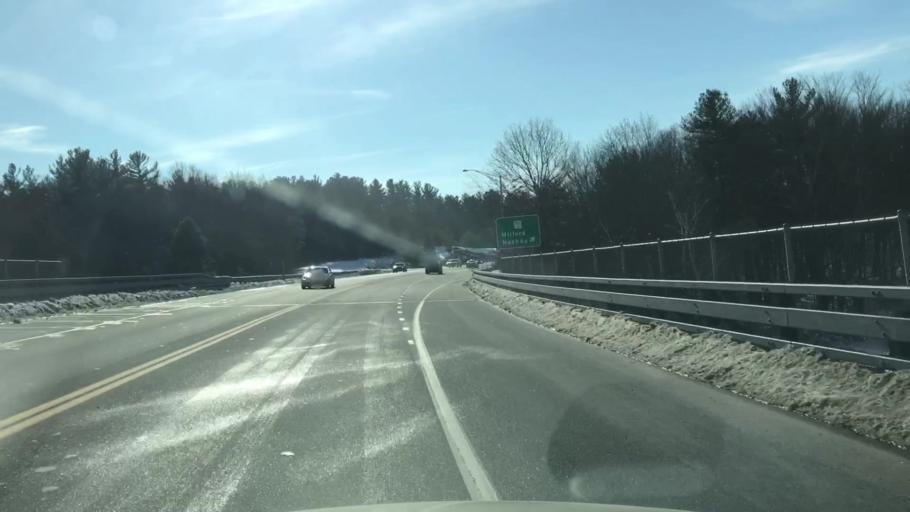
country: US
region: New Hampshire
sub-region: Hillsborough County
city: Milford
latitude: 42.8248
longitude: -71.6173
